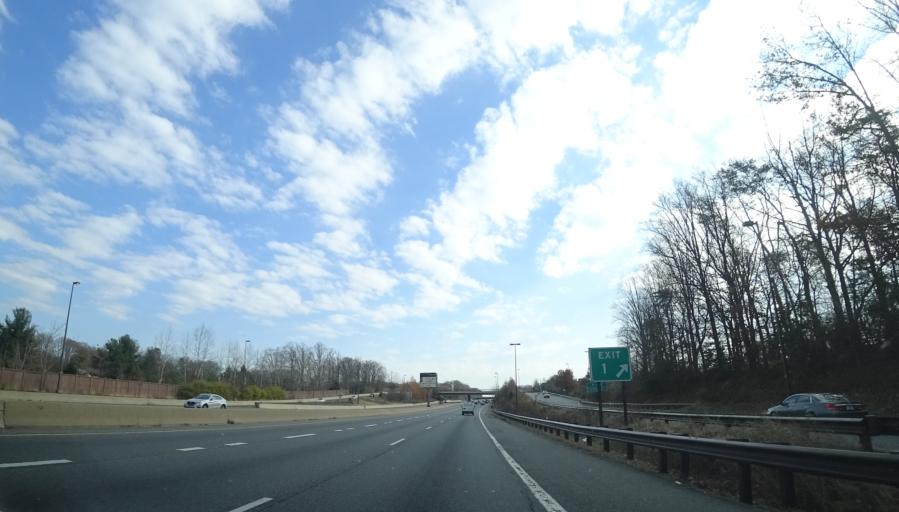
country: US
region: Maryland
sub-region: Montgomery County
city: North Bethesda
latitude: 39.0321
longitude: -77.1354
